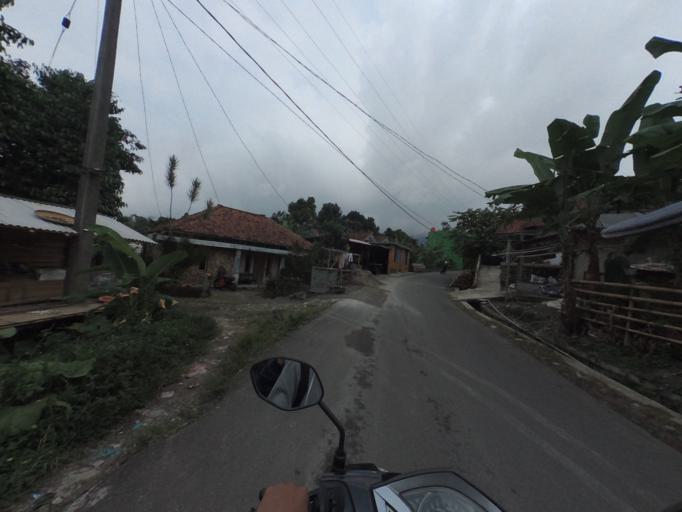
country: ID
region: West Java
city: Ciampea
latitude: -6.6828
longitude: 106.6611
